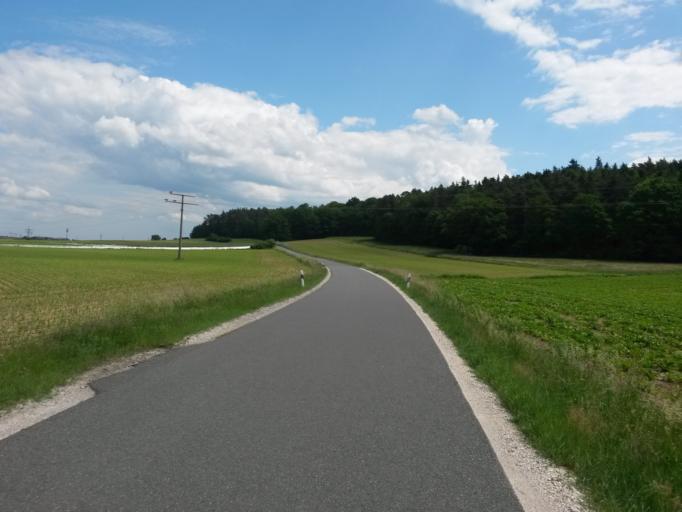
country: DE
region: Bavaria
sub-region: Regierungsbezirk Mittelfranken
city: Oberasbach
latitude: 49.4247
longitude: 10.9211
